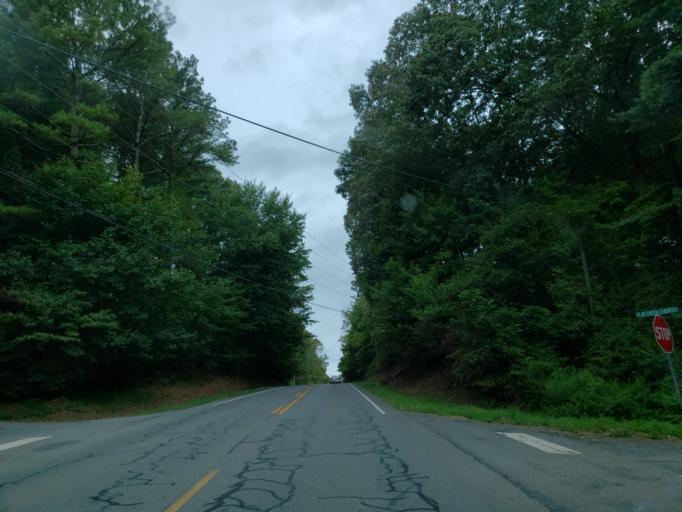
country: US
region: Georgia
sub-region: Gilmer County
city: Ellijay
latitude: 34.6404
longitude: -84.5628
